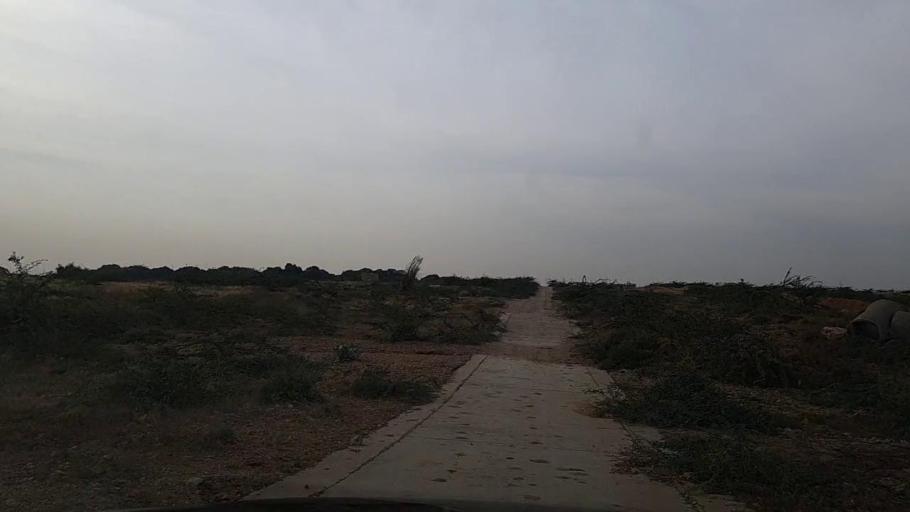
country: PK
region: Sindh
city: Gharo
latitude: 24.7908
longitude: 67.5493
